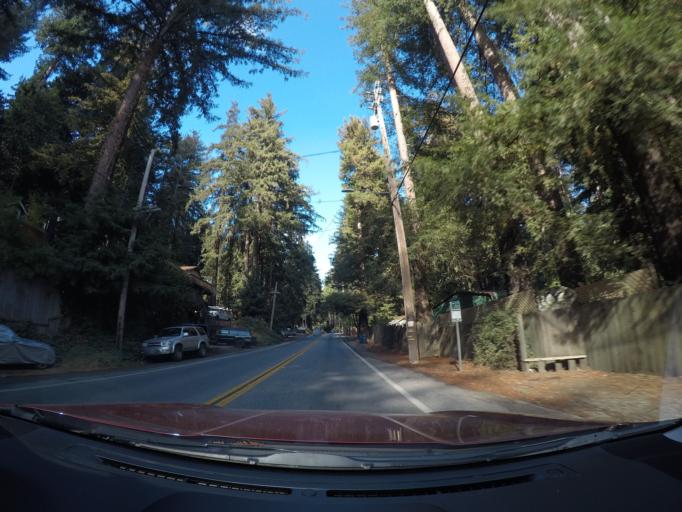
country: US
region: California
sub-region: Santa Cruz County
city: Brookdale
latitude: 37.1065
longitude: -122.1067
